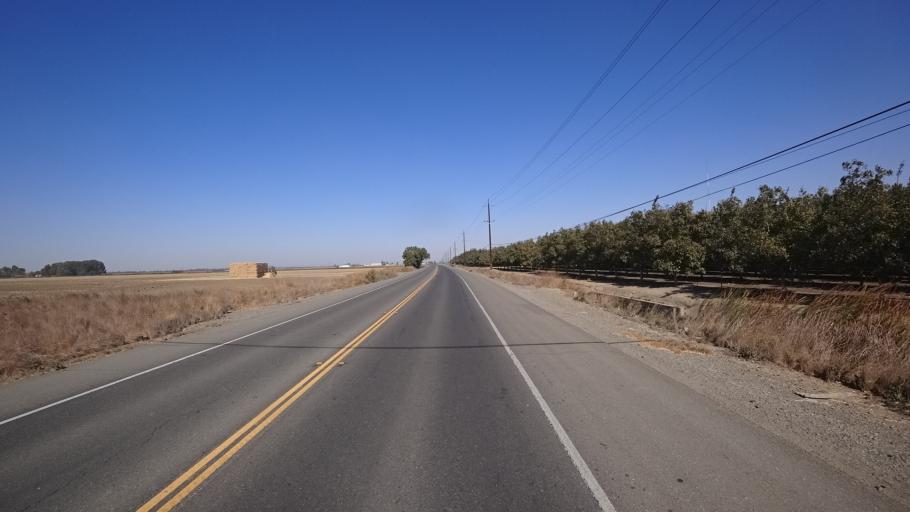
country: US
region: California
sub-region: Yolo County
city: Davis
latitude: 38.5842
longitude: -121.7304
